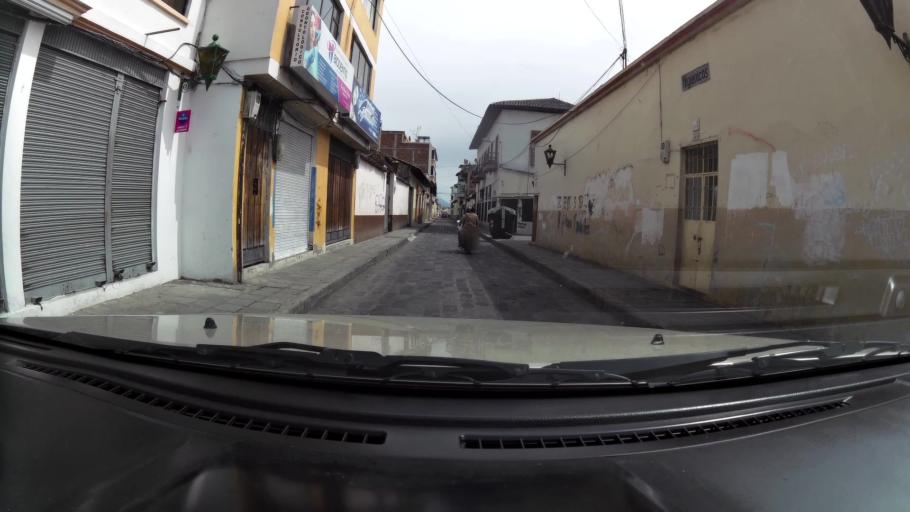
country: EC
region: Cotopaxi
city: Latacunga
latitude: -0.9281
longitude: -78.6154
